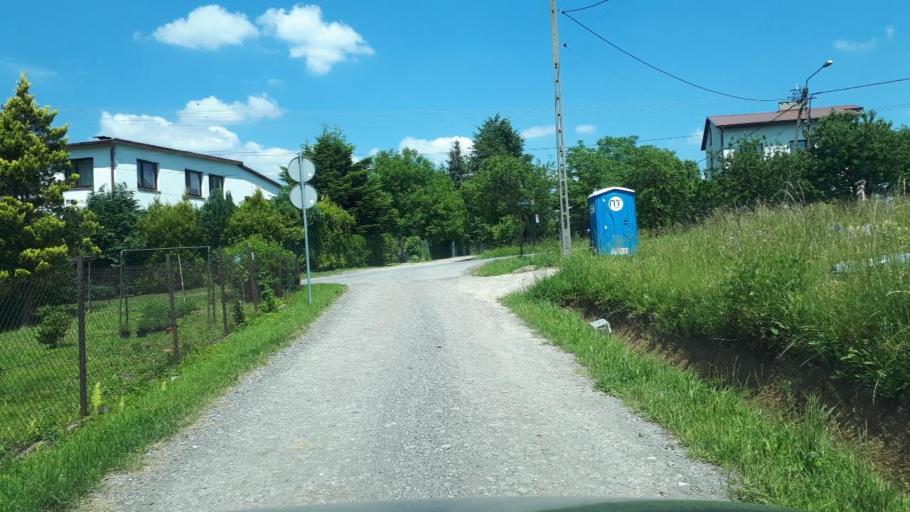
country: PL
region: Silesian Voivodeship
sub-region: Powiat bielski
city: Kozy
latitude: 49.8433
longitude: 19.1597
